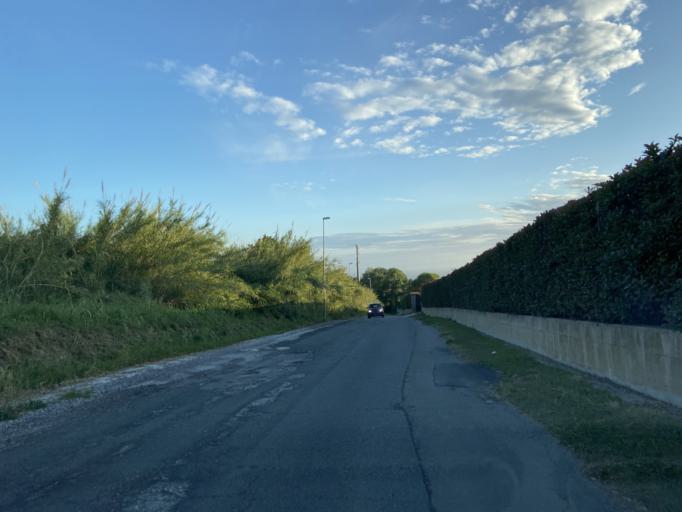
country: IT
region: Latium
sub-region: Citta metropolitana di Roma Capitale
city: Civitavecchia
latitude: 42.0795
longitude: 11.8268
